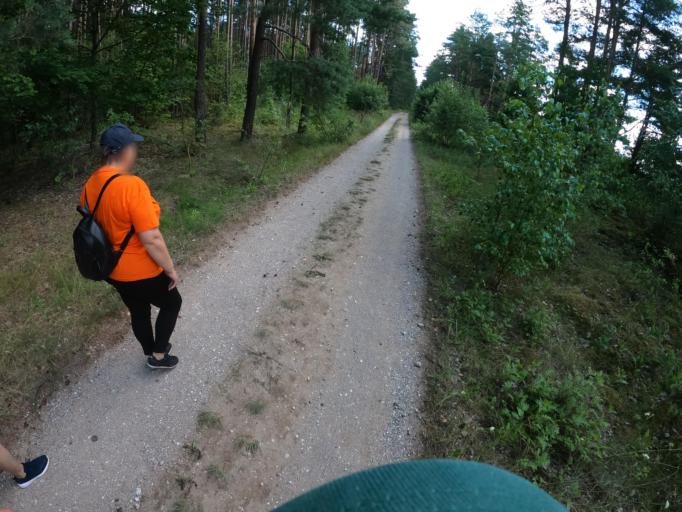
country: LT
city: Birstonas
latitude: 54.6523
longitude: 24.0857
